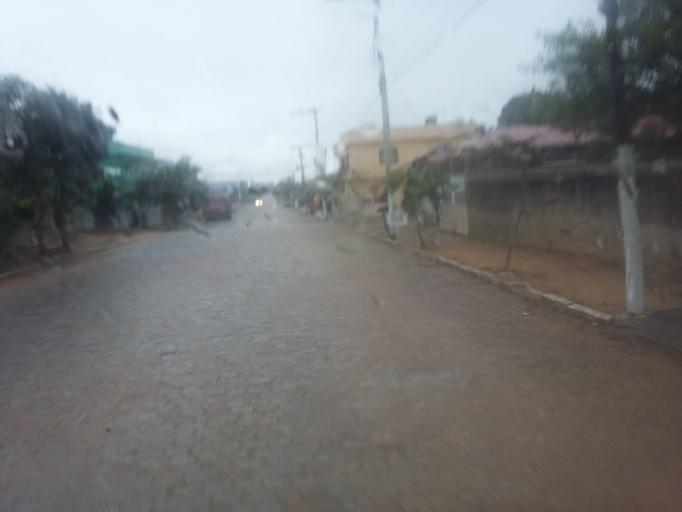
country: BR
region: Rio Grande do Sul
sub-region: Camaqua
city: Camaqua
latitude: -30.8399
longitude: -51.8152
